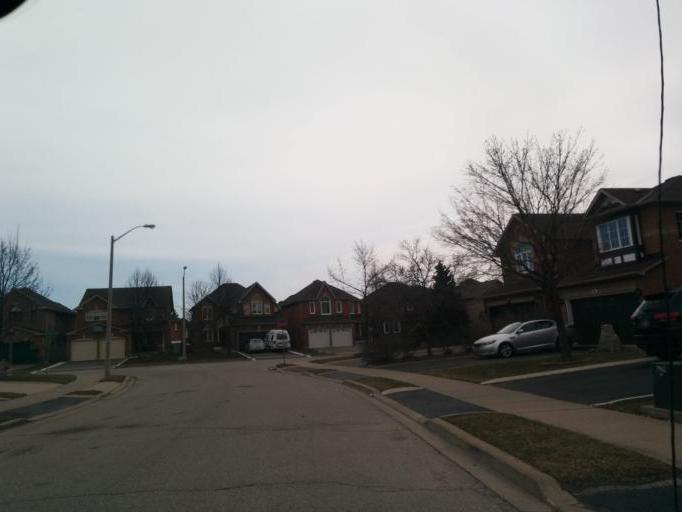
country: CA
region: Ontario
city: Brampton
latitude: 43.7291
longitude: -79.8232
